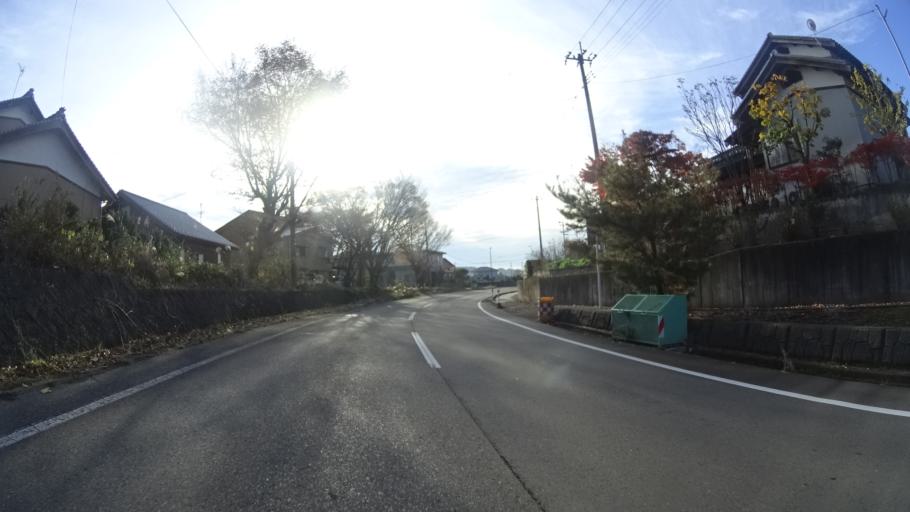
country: JP
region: Niigata
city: Yoshida-kasugacho
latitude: 37.6997
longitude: 138.8346
